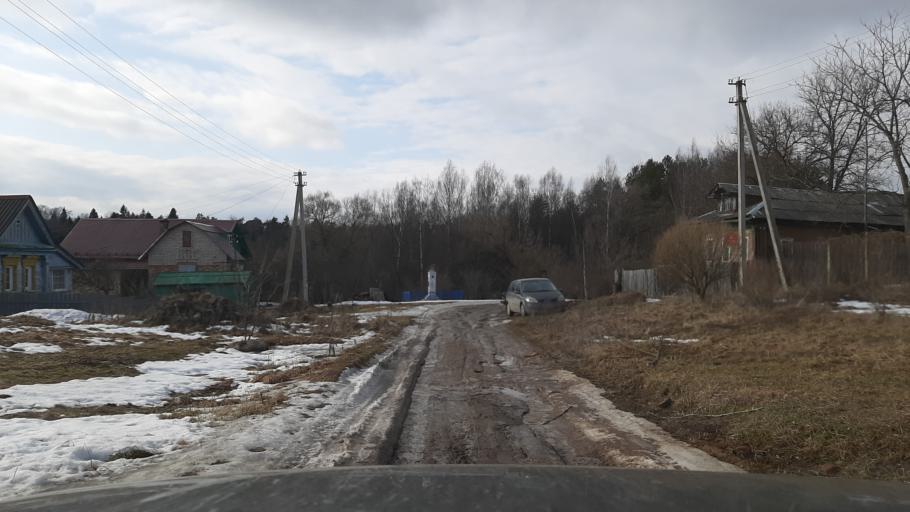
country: RU
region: Ivanovo
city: Teykovo
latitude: 56.8990
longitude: 40.6782
